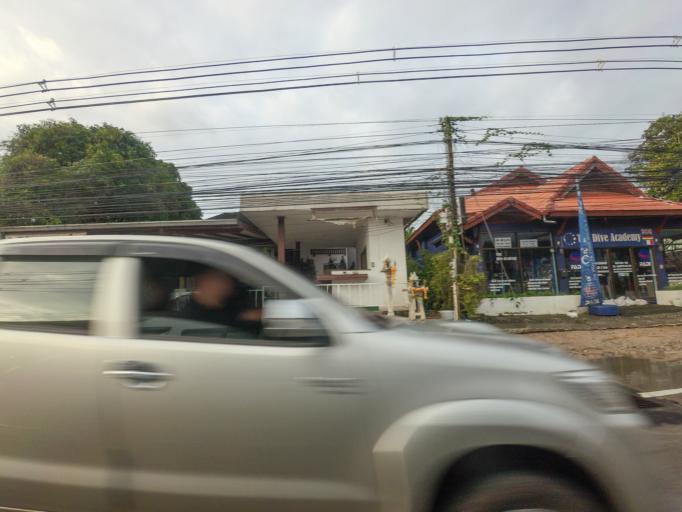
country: TH
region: Surat Thani
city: Ko Samui
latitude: 9.5593
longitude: 100.0252
